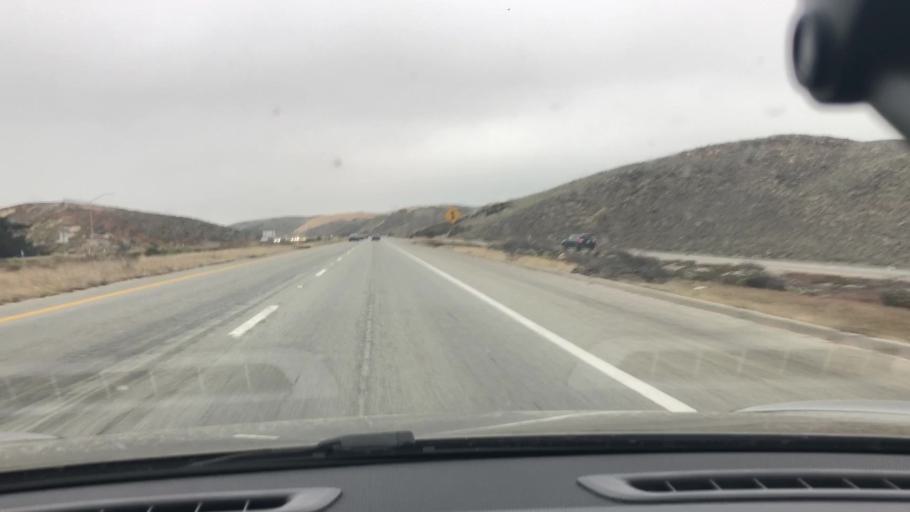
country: US
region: California
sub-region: Monterey County
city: Marina
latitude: 36.6957
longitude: -121.8058
